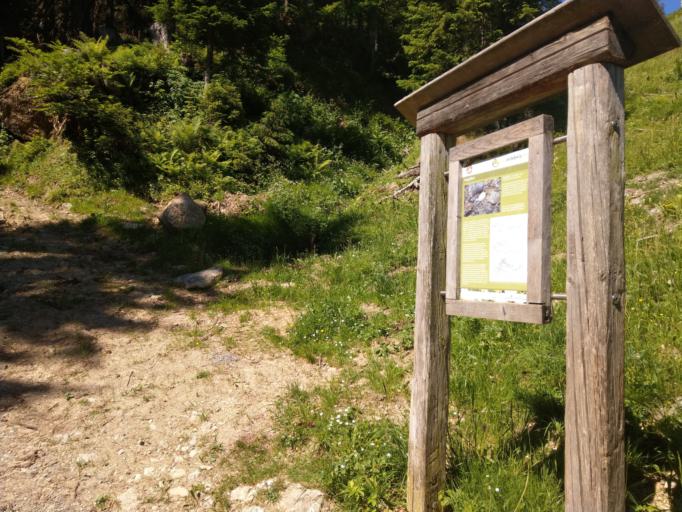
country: AT
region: Vorarlberg
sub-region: Politischer Bezirk Bregenz
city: Riefensberg
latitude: 47.5072
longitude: 10.0111
